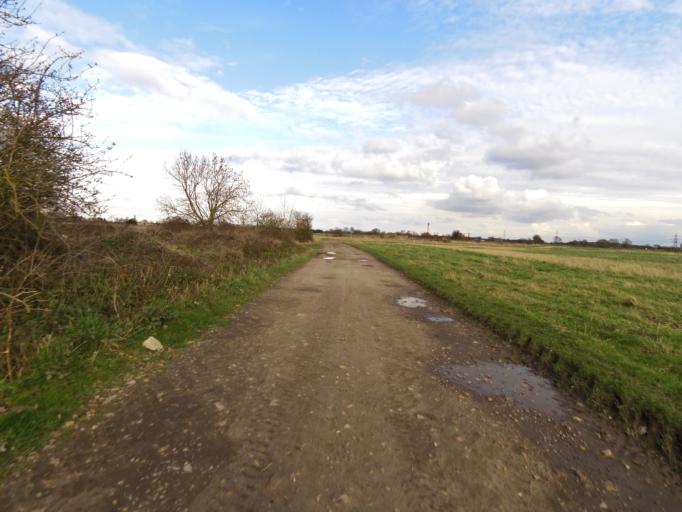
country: GB
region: England
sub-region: North Yorkshire
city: Brayton
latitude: 53.7381
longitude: -1.0881
